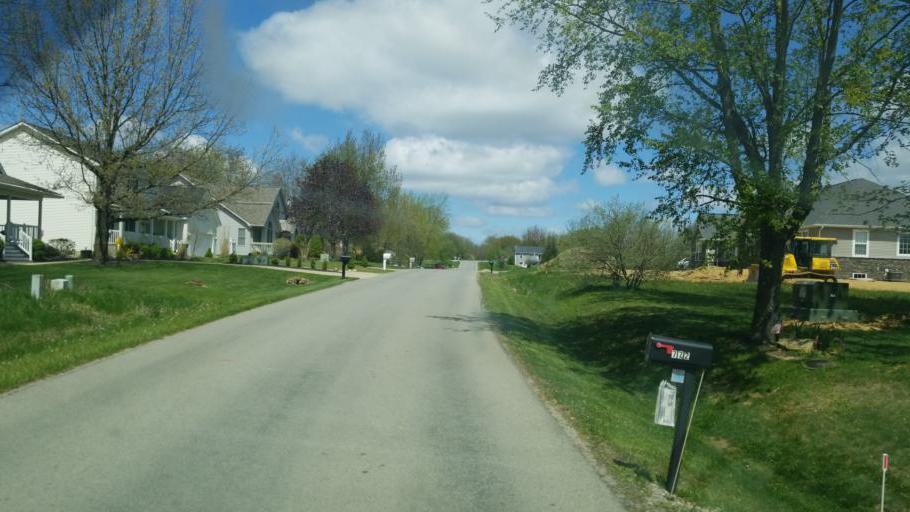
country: US
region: Ohio
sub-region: Knox County
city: Gambier
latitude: 40.4406
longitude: -82.3612
